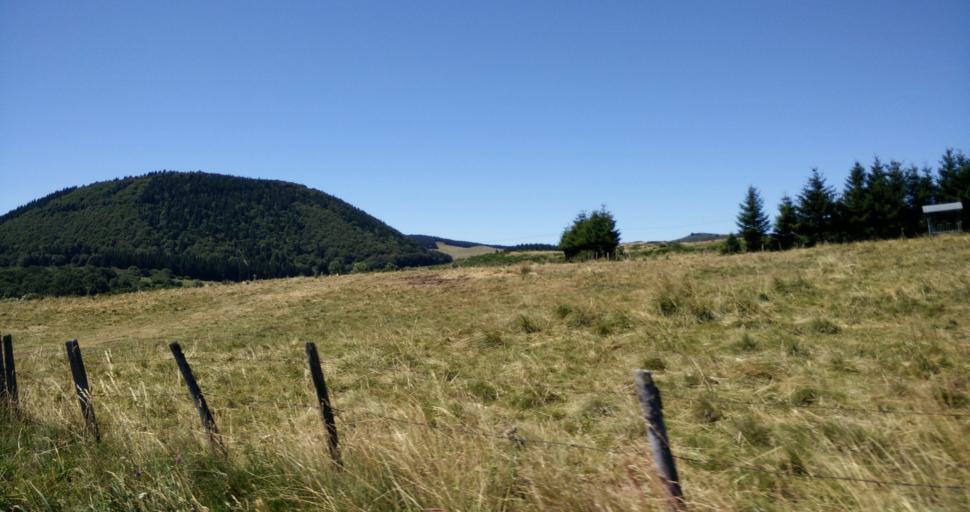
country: FR
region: Auvergne
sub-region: Departement du Puy-de-Dome
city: Mont-Dore
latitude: 45.4685
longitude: 2.9164
